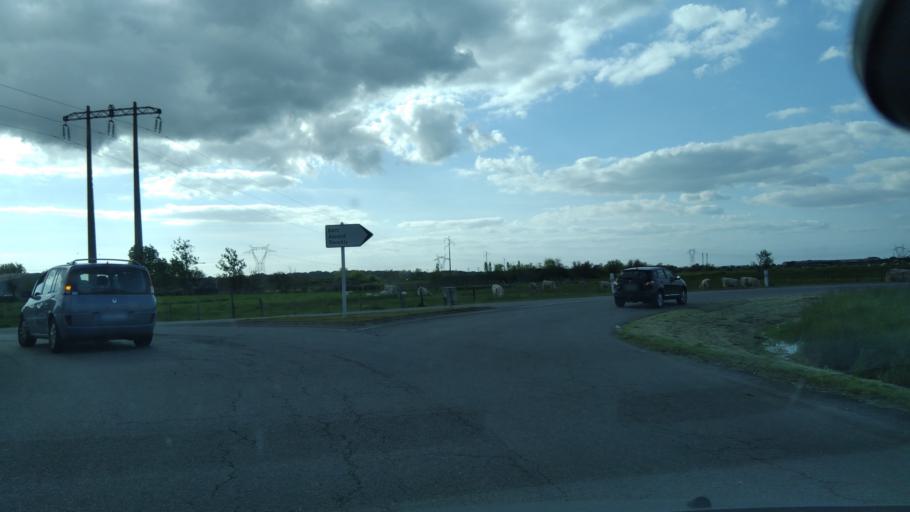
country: FR
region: Pays de la Loire
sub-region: Departement de la Loire-Atlantique
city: Saint-Nazaire
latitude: 47.2982
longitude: -2.2198
